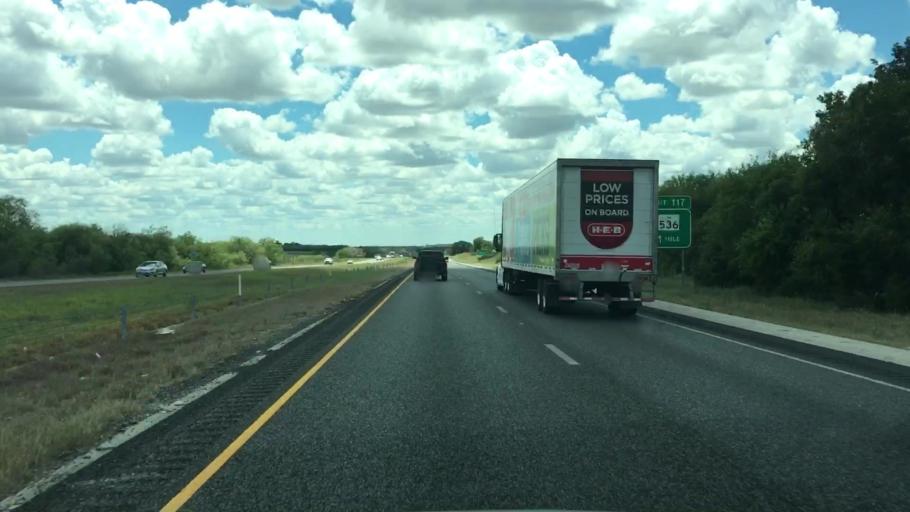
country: US
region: Texas
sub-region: Atascosa County
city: Poteet
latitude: 29.1246
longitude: -98.4311
